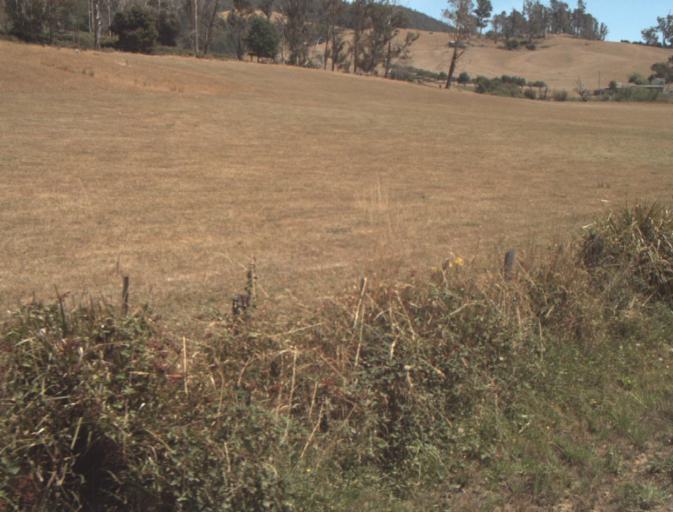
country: AU
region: Tasmania
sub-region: Launceston
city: Mayfield
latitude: -41.2577
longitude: 147.1335
